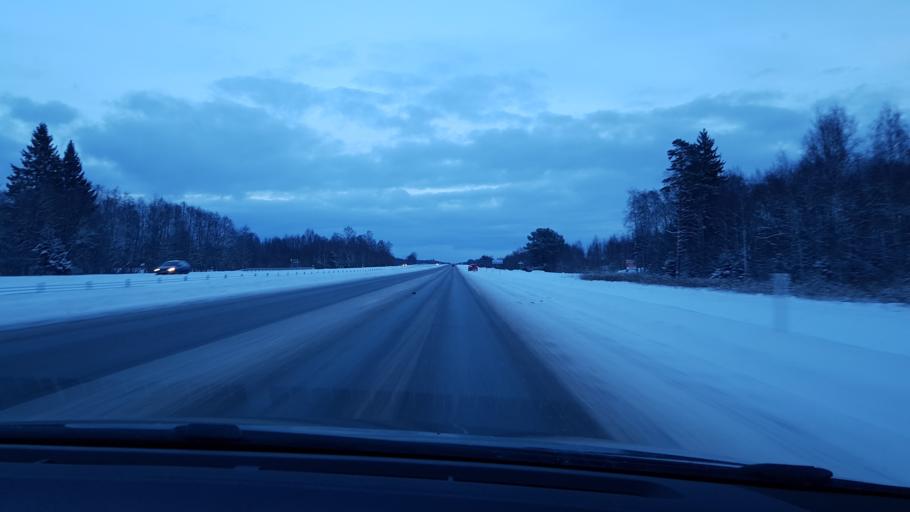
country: EE
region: Harju
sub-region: Anija vald
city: Kehra
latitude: 59.4404
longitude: 25.2922
